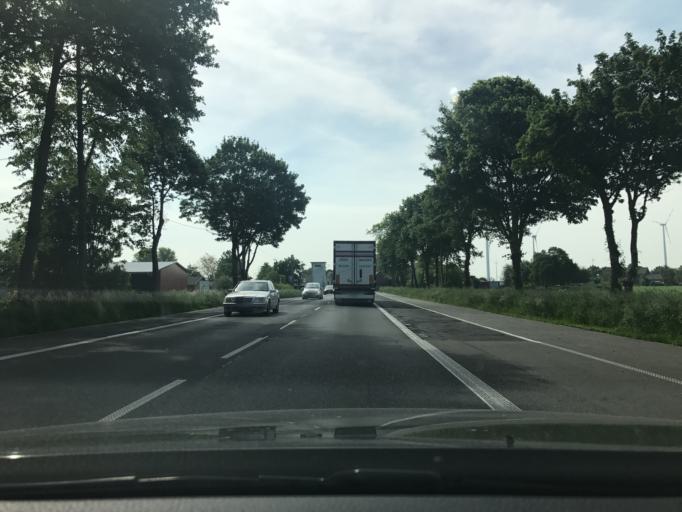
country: DE
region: North Rhine-Westphalia
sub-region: Regierungsbezirk Dusseldorf
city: Grefrath
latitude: 51.3616
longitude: 6.3156
